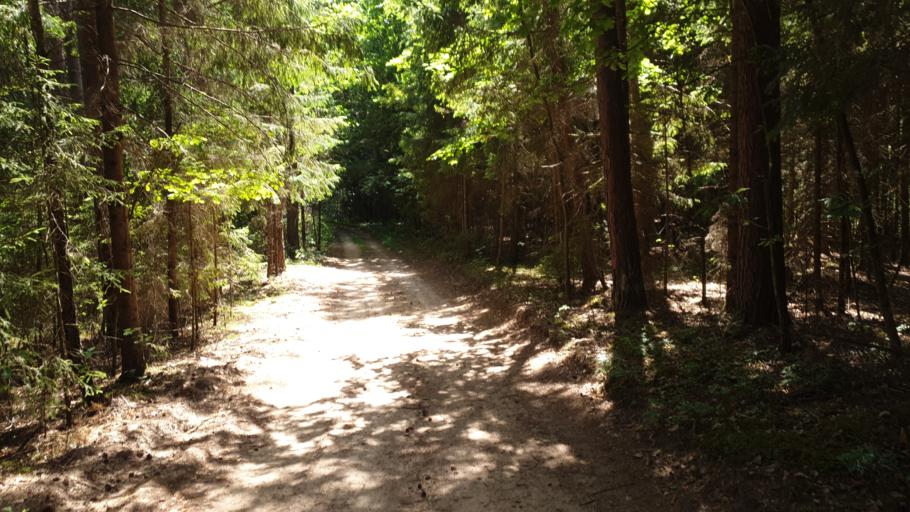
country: LT
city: Grigiskes
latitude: 54.7784
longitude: 24.9935
